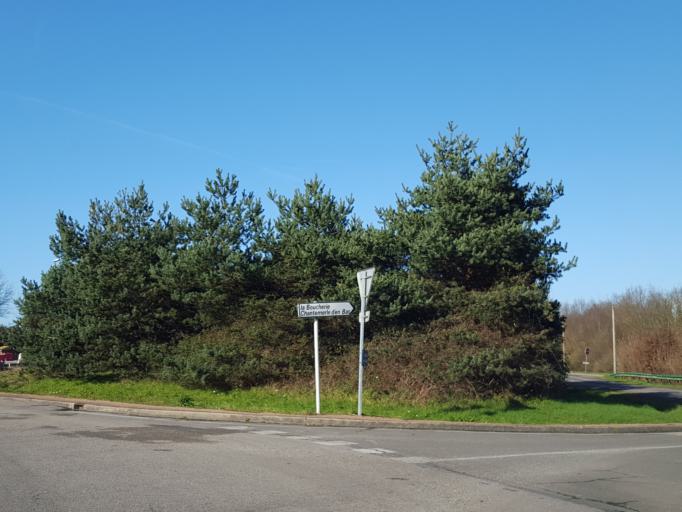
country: FR
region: Pays de la Loire
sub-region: Departement de la Vendee
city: La Roche-sur-Yon
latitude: 46.6623
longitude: -1.4617
